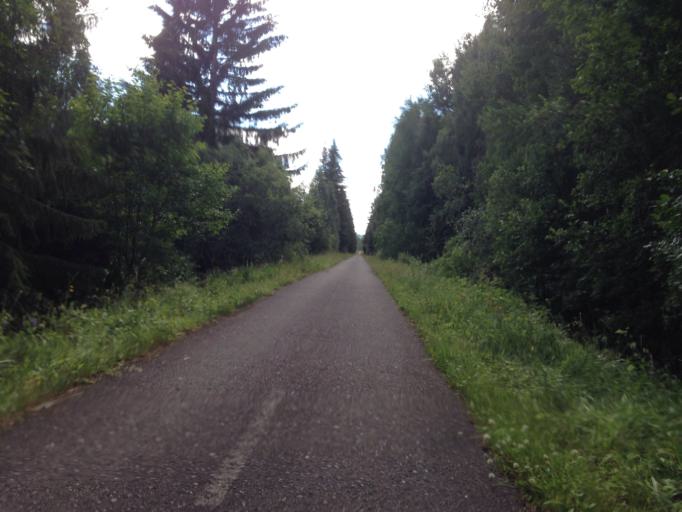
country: SE
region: Dalarna
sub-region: Ludvika Kommun
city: Ludvika
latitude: 60.2045
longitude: 15.1034
